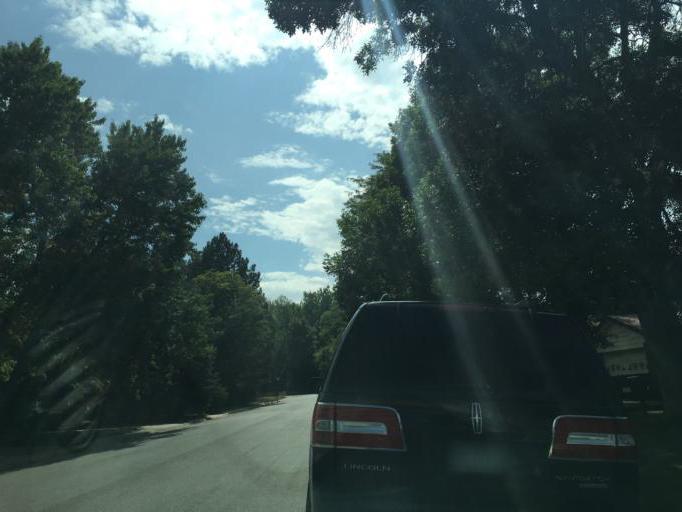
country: US
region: Colorado
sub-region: Jefferson County
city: Applewood
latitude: 39.7592
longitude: -105.1319
